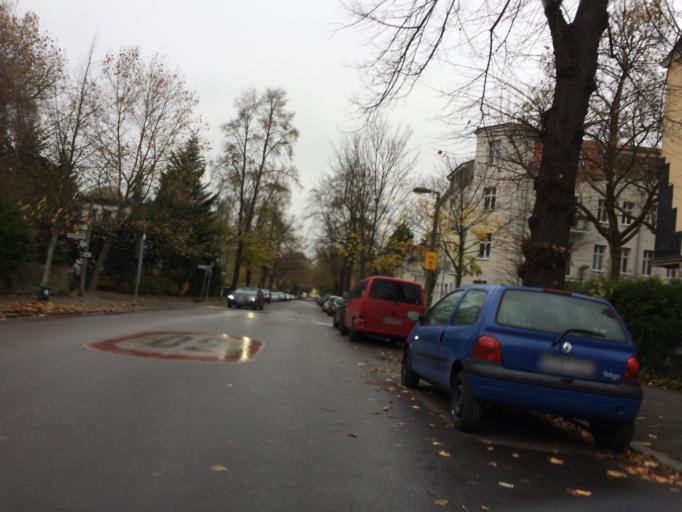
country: DE
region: Berlin
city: Niederschonhausen
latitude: 52.5845
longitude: 13.3982
